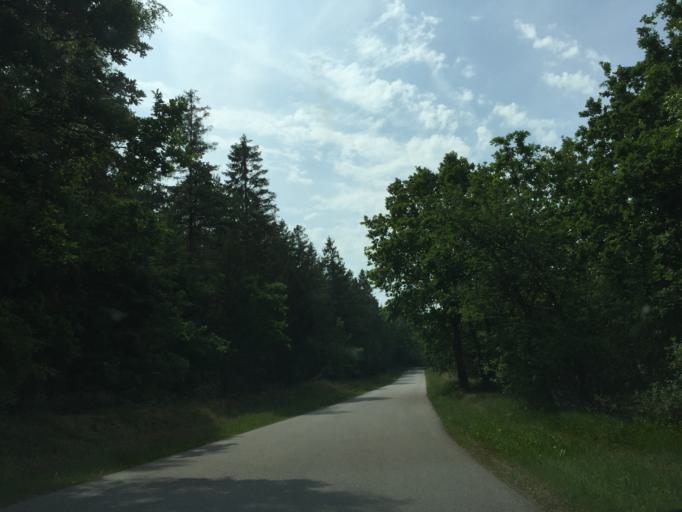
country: DK
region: Central Jutland
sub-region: Silkeborg Kommune
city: Virklund
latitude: 56.0539
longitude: 9.4574
